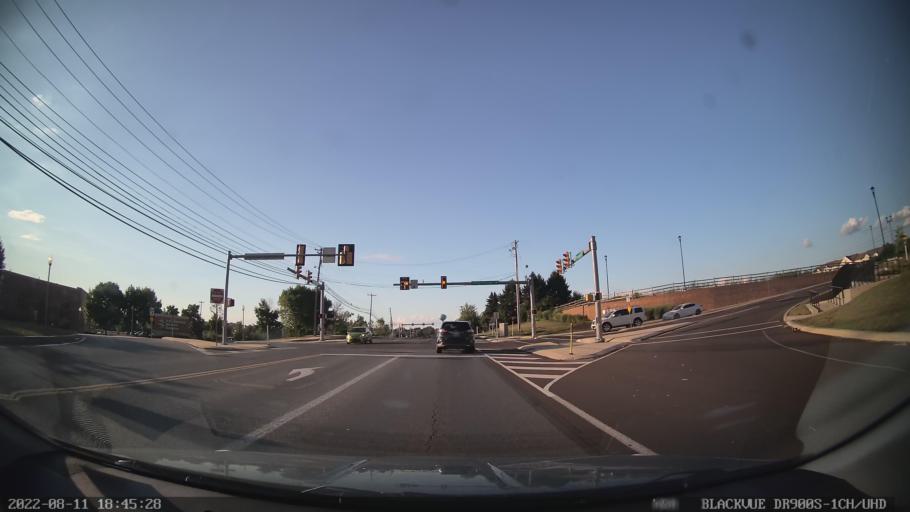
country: US
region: Pennsylvania
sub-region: Lehigh County
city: Wescosville
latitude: 40.5834
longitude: -75.5576
